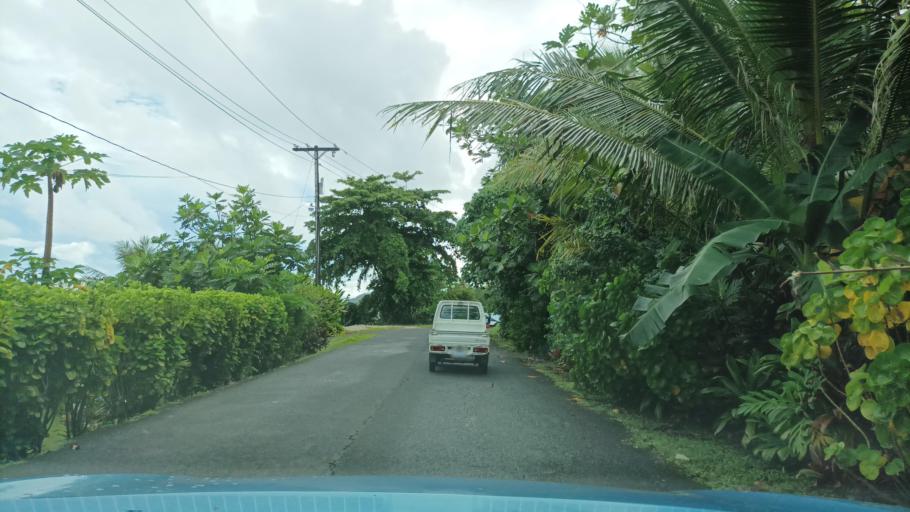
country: FM
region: Pohnpei
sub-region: Kolonia Municipality
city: Kolonia
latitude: 6.9695
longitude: 158.2546
